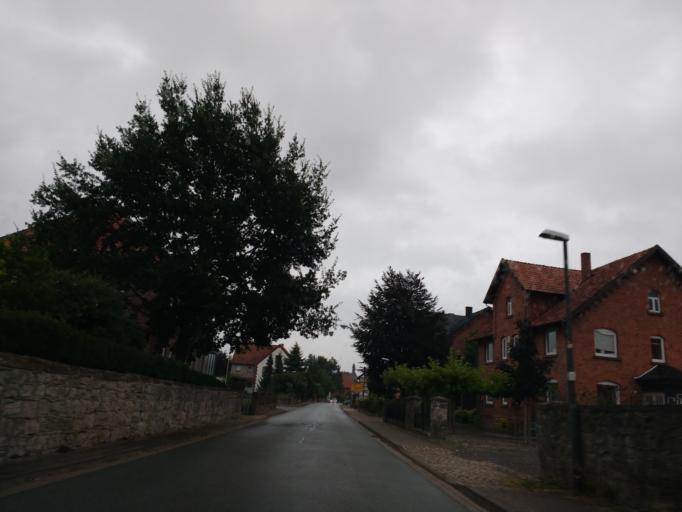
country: DE
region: Lower Saxony
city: Hehlen
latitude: 52.0325
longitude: 9.4580
